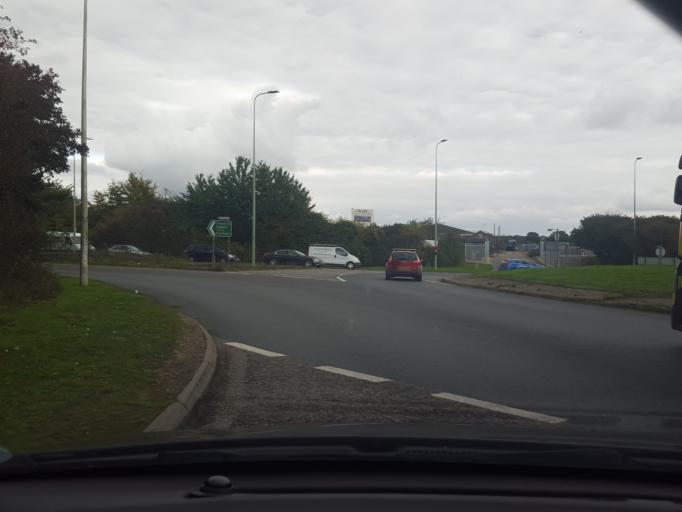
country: GB
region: England
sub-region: Suffolk
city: Bury St Edmunds
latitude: 52.2622
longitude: 0.7247
